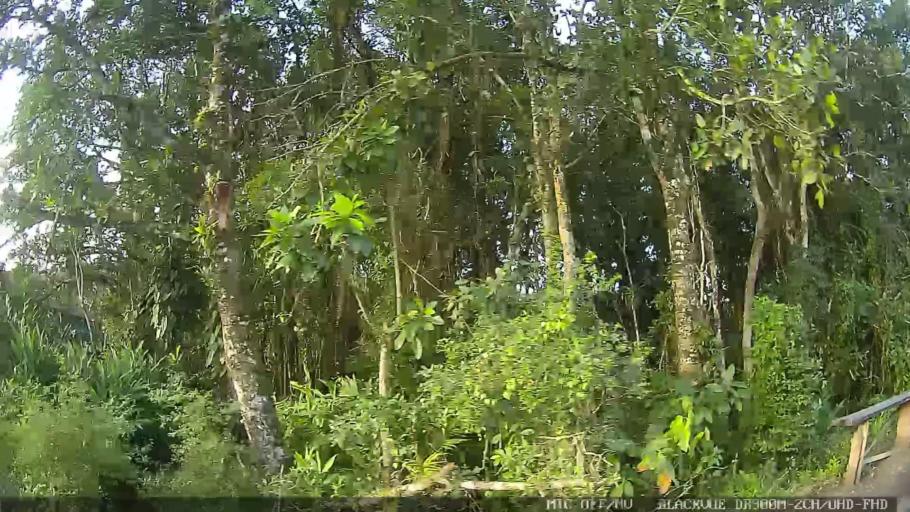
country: BR
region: Sao Paulo
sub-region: Itanhaem
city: Itanhaem
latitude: -24.1344
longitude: -46.7213
